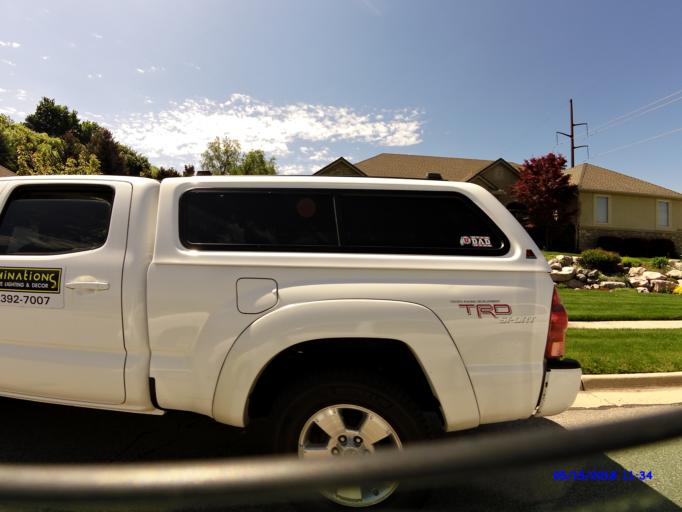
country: US
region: Utah
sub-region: Weber County
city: South Ogden
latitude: 41.1774
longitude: -111.9393
